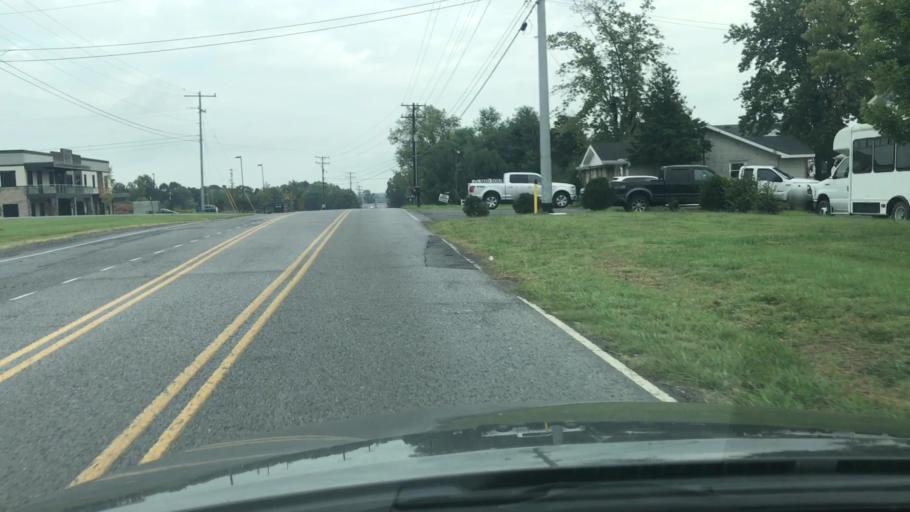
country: US
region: Tennessee
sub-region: Sumner County
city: White House
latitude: 36.4631
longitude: -86.6752
